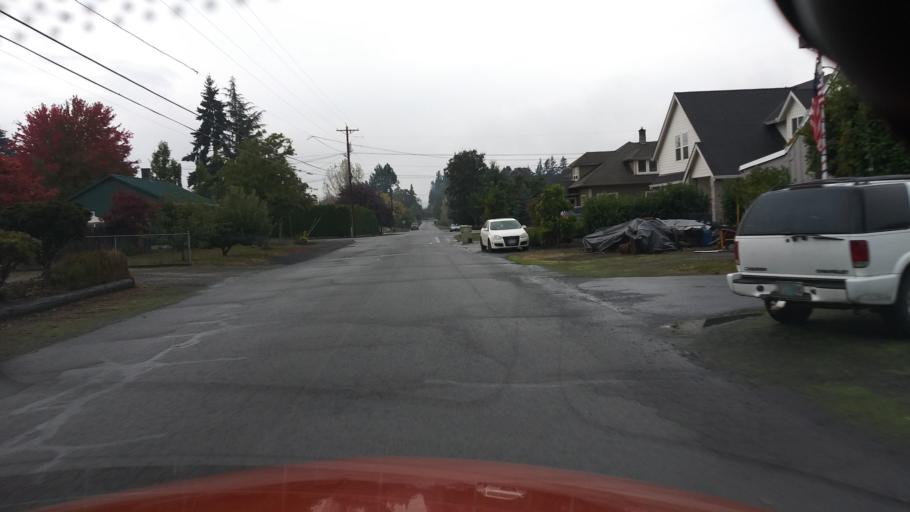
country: US
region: Oregon
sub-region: Washington County
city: North Plains
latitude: 45.5963
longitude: -123.0011
